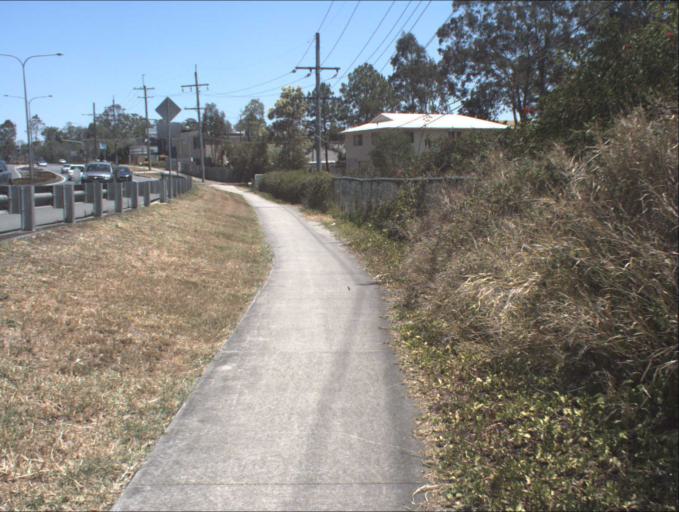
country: AU
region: Queensland
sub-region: Logan
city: Slacks Creek
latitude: -27.6722
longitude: 153.1859
